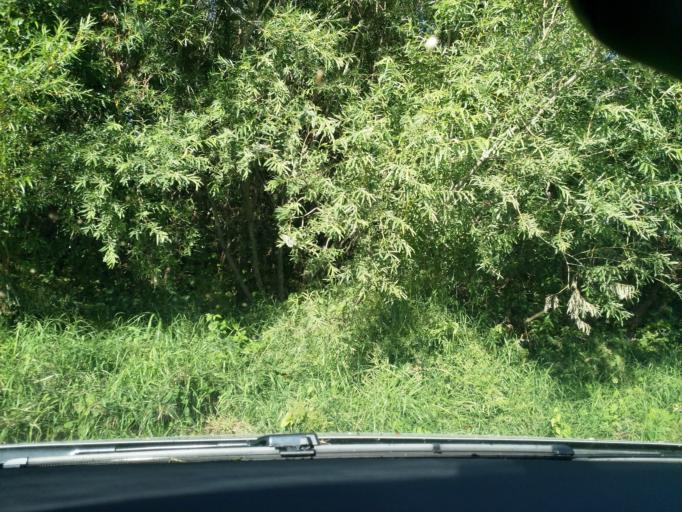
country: LV
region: Kuldigas Rajons
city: Kuldiga
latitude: 56.9760
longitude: 21.9732
